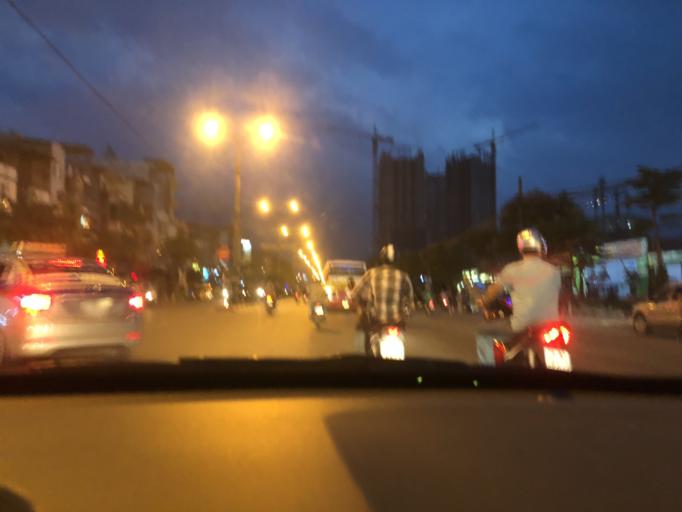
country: VN
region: Ha Noi
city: Hai BaTrung
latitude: 20.9898
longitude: 105.8411
